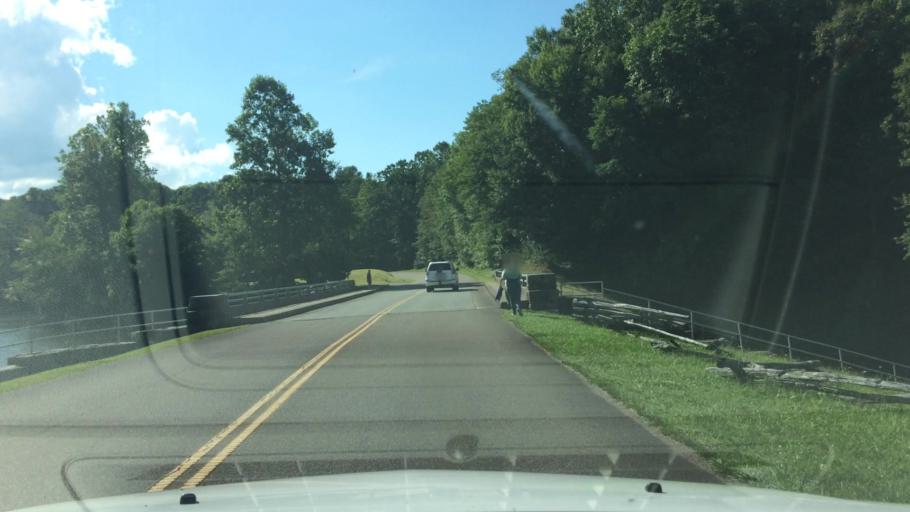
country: US
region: North Carolina
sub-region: Watauga County
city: Foscoe
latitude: 36.1385
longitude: -81.7311
